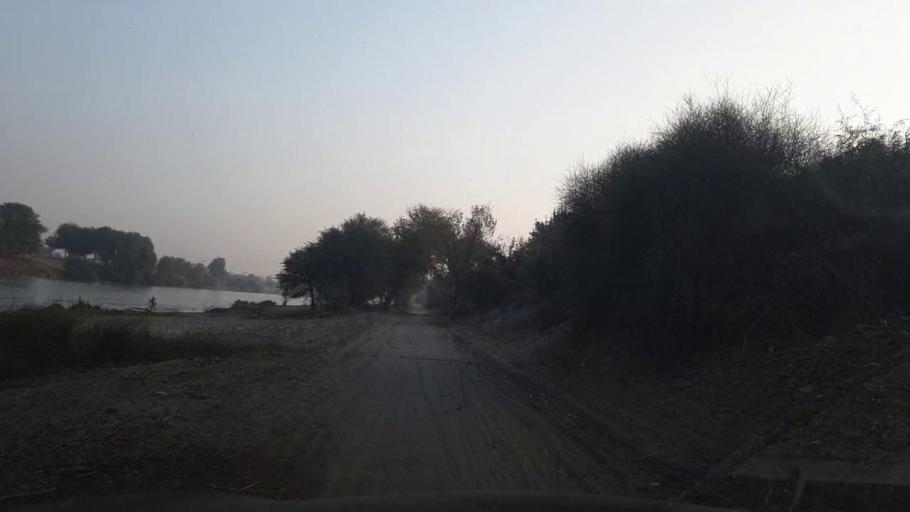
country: PK
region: Sindh
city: Ubauro
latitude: 28.3091
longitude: 69.7898
